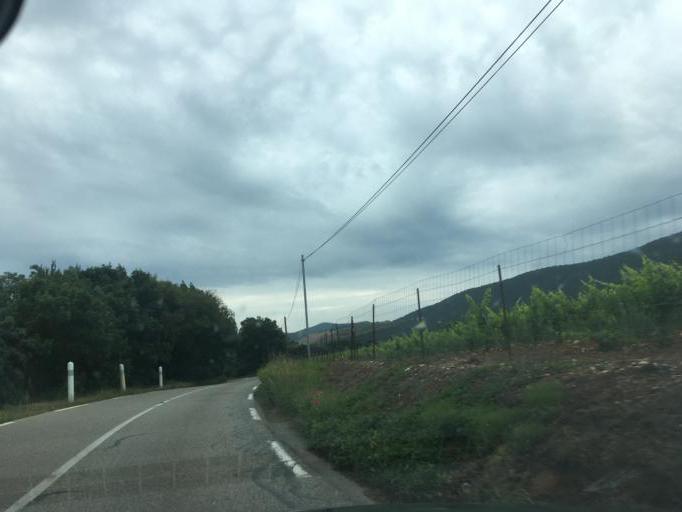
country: FR
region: Provence-Alpes-Cote d'Azur
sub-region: Departement du Var
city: Pierrefeu-du-Var
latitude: 43.2335
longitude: 6.1910
